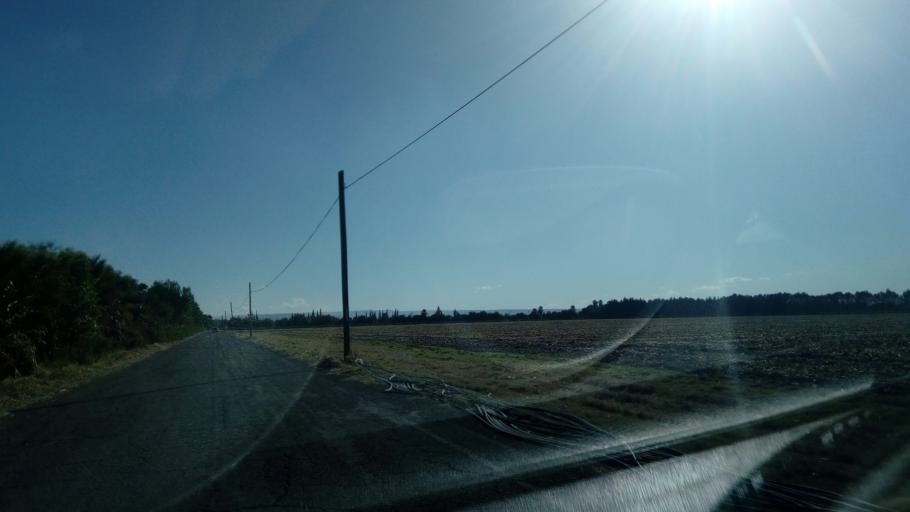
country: MX
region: Durango
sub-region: Durango
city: Jose Refugio Salcido
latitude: 24.0086
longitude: -104.5486
